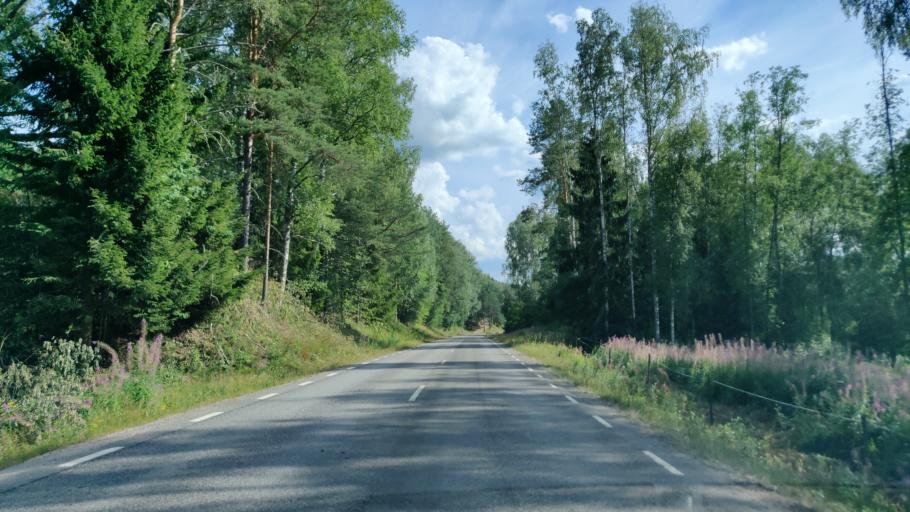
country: SE
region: Vaermland
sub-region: Hagfors Kommun
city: Ekshaerad
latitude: 60.1751
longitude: 13.5291
